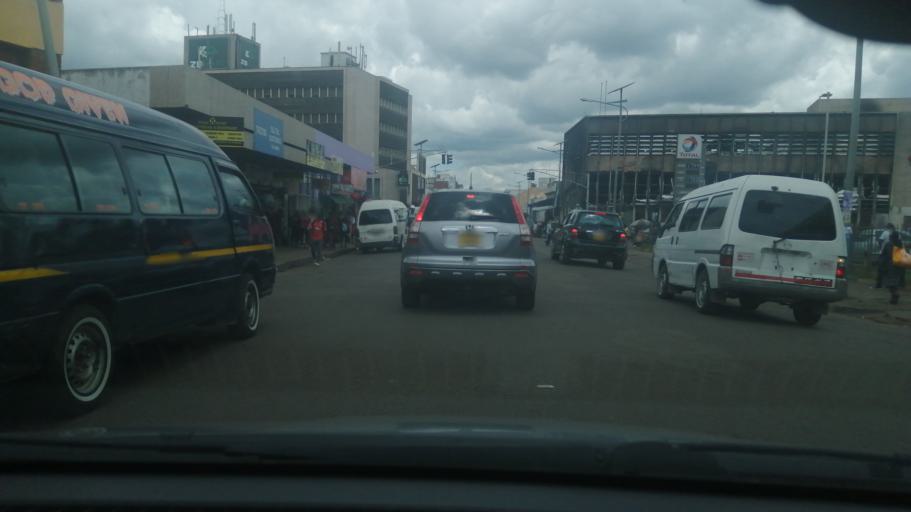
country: ZW
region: Harare
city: Harare
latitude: -17.8343
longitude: 31.0428
